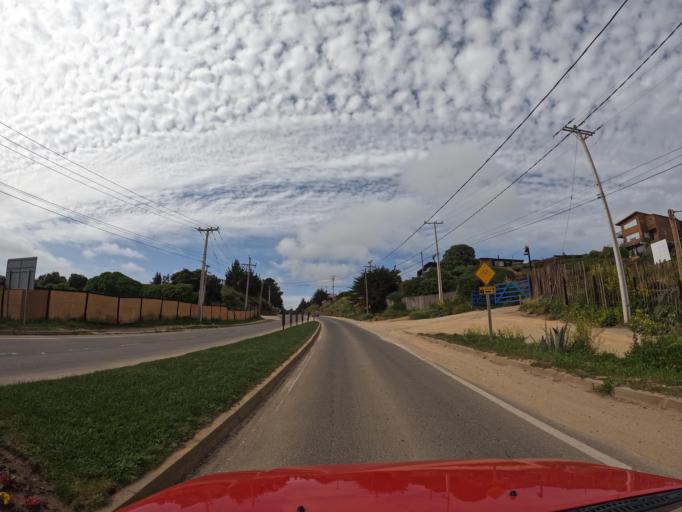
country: CL
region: O'Higgins
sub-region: Provincia de Colchagua
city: Santa Cruz
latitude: -34.4293
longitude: -72.0326
